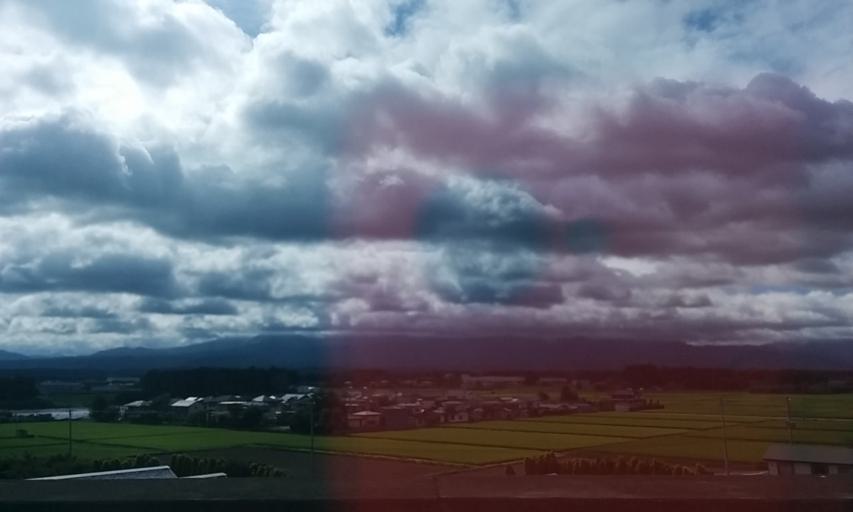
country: JP
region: Tochigi
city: Otawara
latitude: 36.8596
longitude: 139.9690
